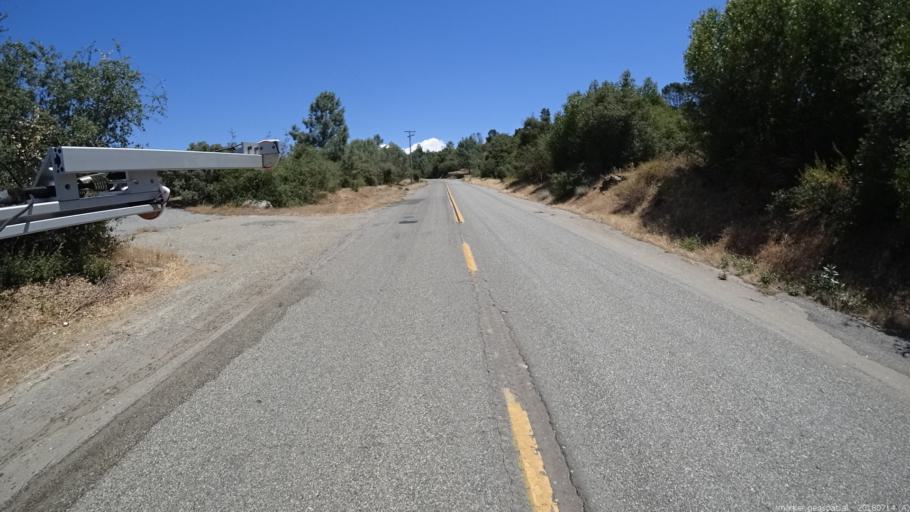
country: US
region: California
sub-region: Madera County
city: Ahwahnee
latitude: 37.3940
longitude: -119.7109
